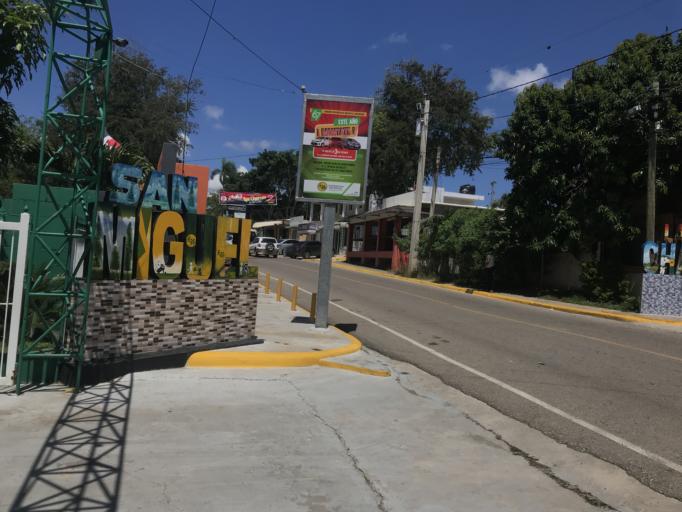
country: DO
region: Santiago
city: Santiago de los Caballeros
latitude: 19.3976
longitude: -70.7434
